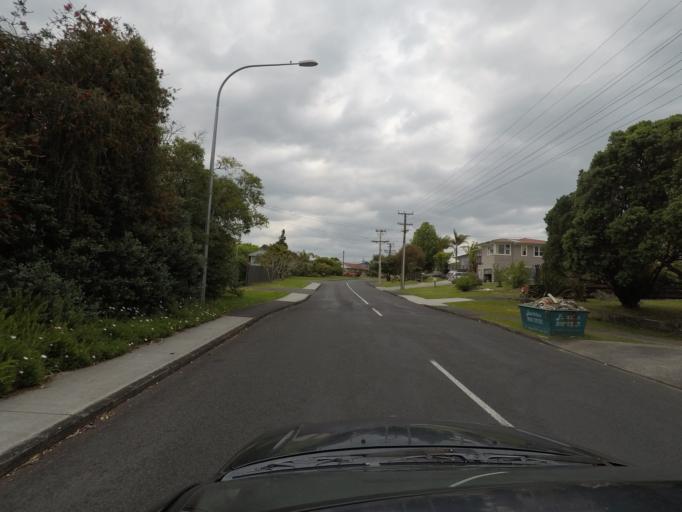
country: NZ
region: Auckland
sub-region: Auckland
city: Rosebank
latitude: -36.8483
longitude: 174.6460
